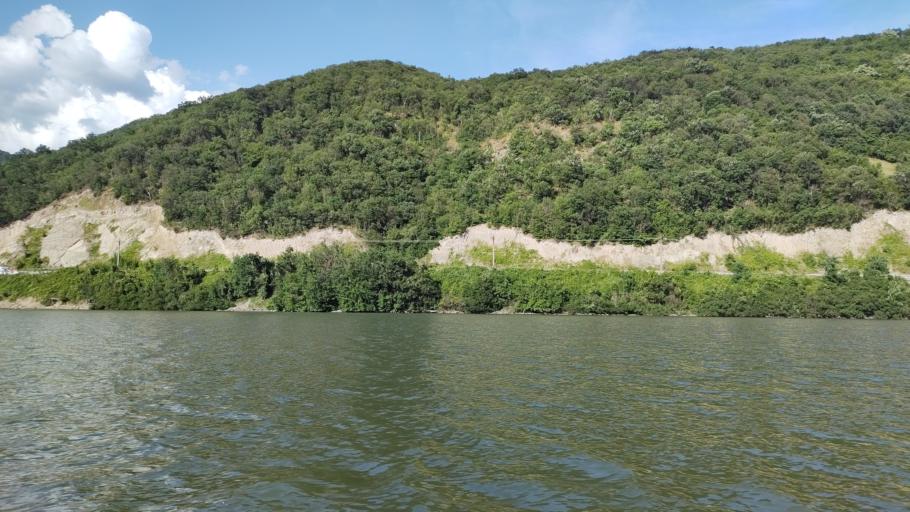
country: RO
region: Mehedinti
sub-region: Comuna Svinita
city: Svinita
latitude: 44.5638
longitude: 22.0304
